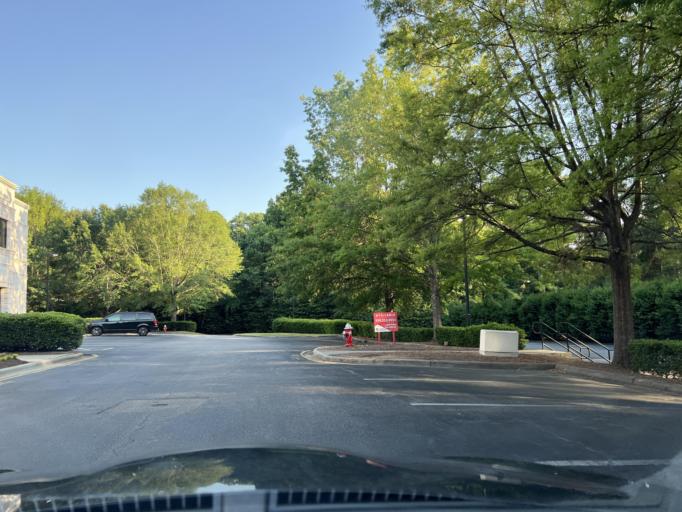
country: US
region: North Carolina
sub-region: Wake County
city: Cary
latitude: 35.7596
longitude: -78.7851
